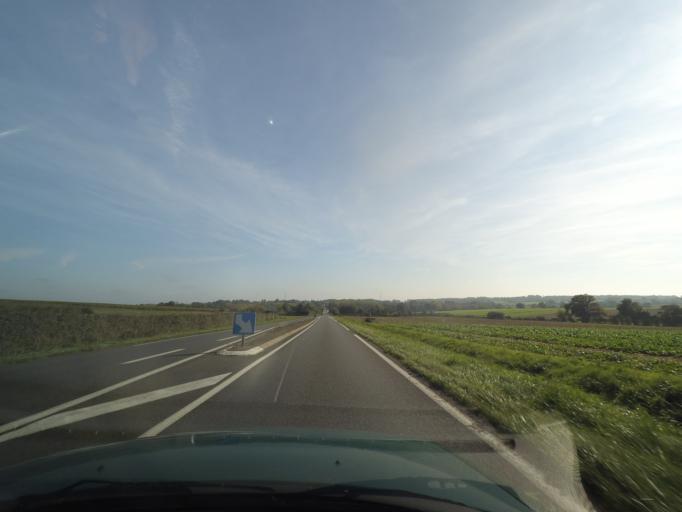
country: FR
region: Pays de la Loire
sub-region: Departement de Maine-et-Loire
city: Vihiers
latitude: 47.1516
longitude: -0.4514
